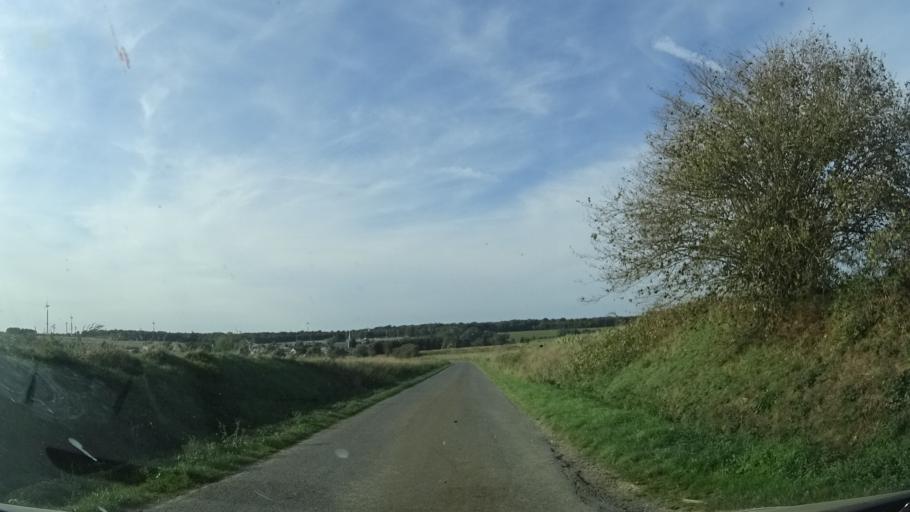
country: BE
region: Wallonia
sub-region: Province de Namur
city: Cerfontaine
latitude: 50.2056
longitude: 4.3643
